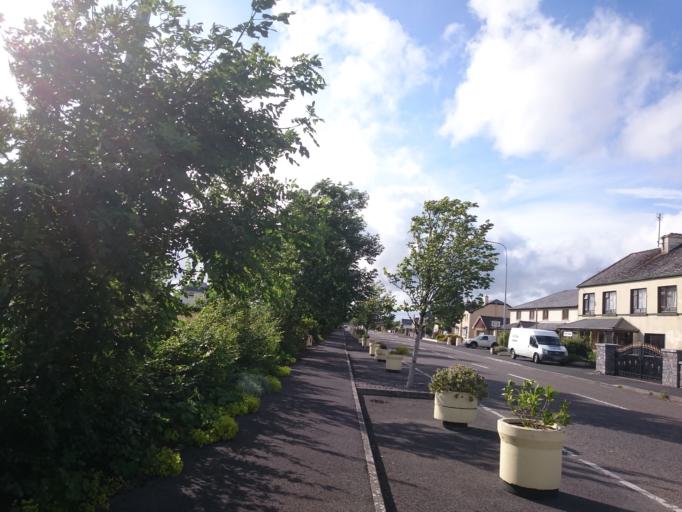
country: IE
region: Connaught
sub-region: Maigh Eo
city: Kiltamagh
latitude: 53.7956
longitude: -8.9197
